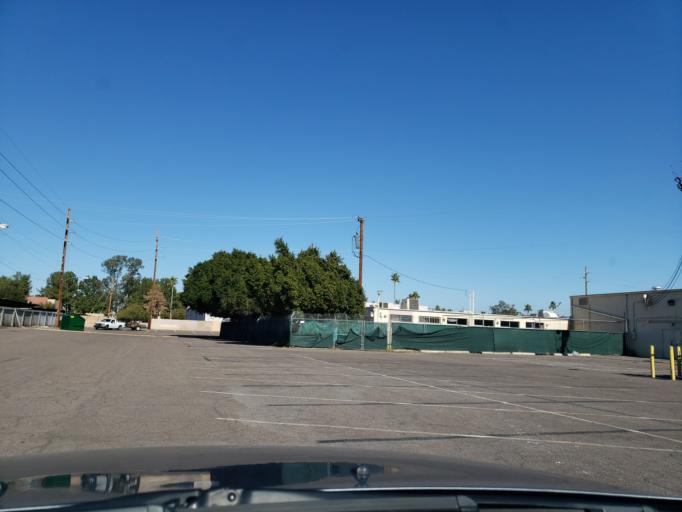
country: US
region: Arizona
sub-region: Maricopa County
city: Paradise Valley
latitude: 33.5834
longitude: -112.0151
